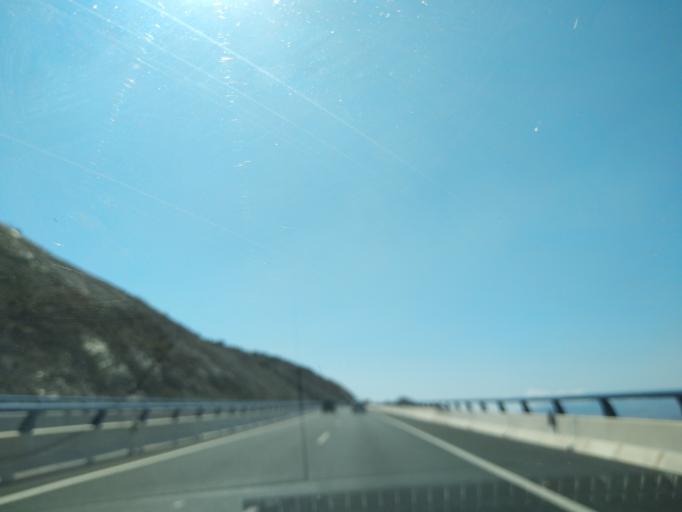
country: ES
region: Andalusia
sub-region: Provincia de Malaga
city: Almogia
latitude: 36.8531
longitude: -4.4848
